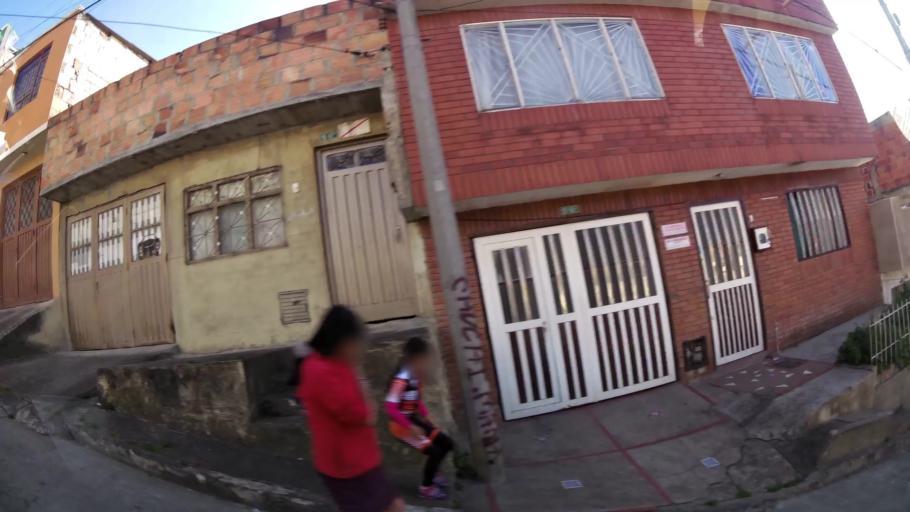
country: CO
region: Bogota D.C.
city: Bogota
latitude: 4.5395
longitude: -74.0908
